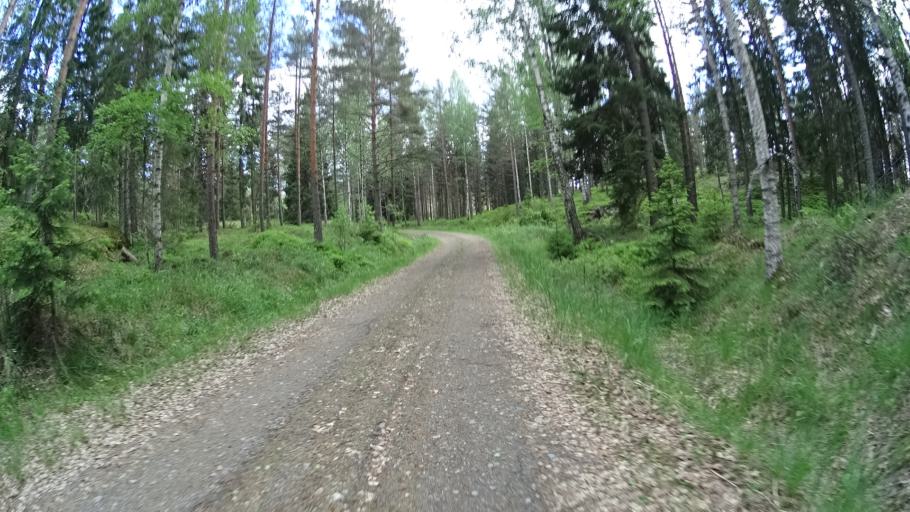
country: FI
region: Varsinais-Suomi
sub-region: Salo
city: Kisko
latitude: 60.1856
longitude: 23.5511
